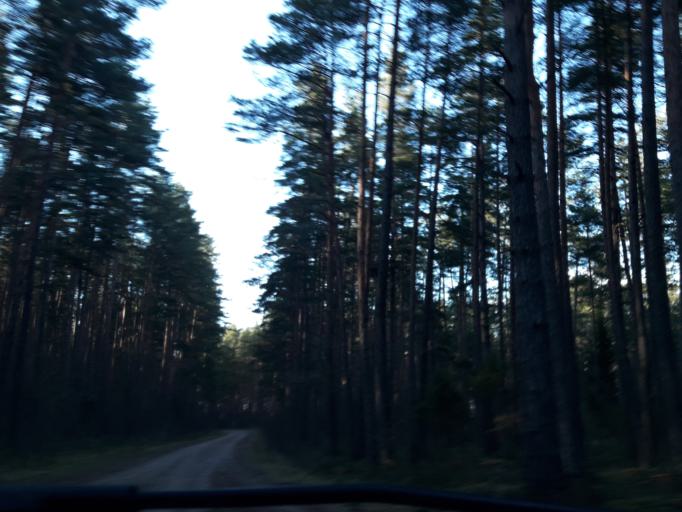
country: LV
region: Kekava
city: Kekava
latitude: 56.8658
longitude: 24.2214
